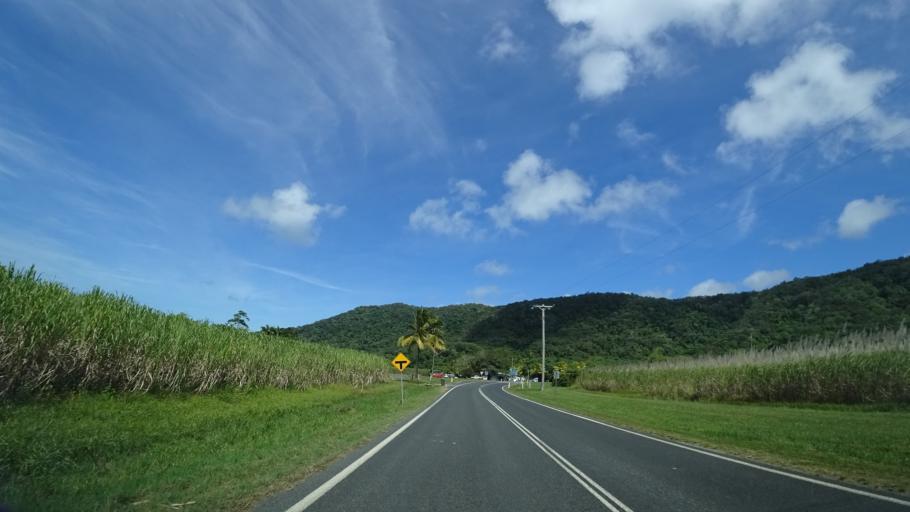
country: AU
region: Queensland
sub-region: Cairns
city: Port Douglas
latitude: -16.2832
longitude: 145.3795
